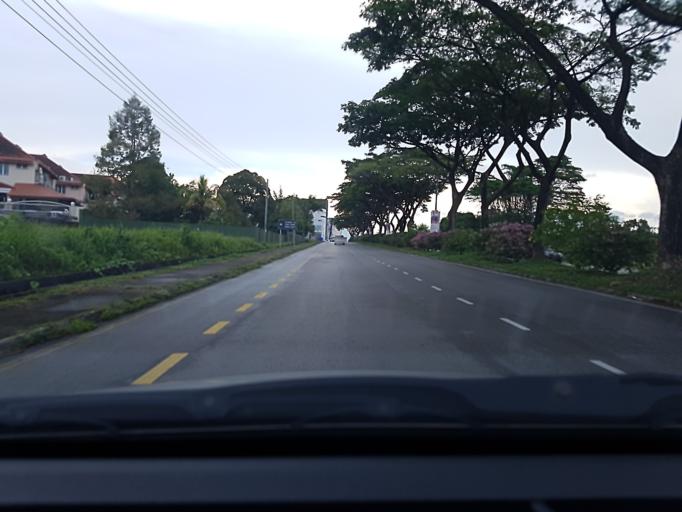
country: MY
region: Sarawak
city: Kuching
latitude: 1.5191
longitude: 110.3594
